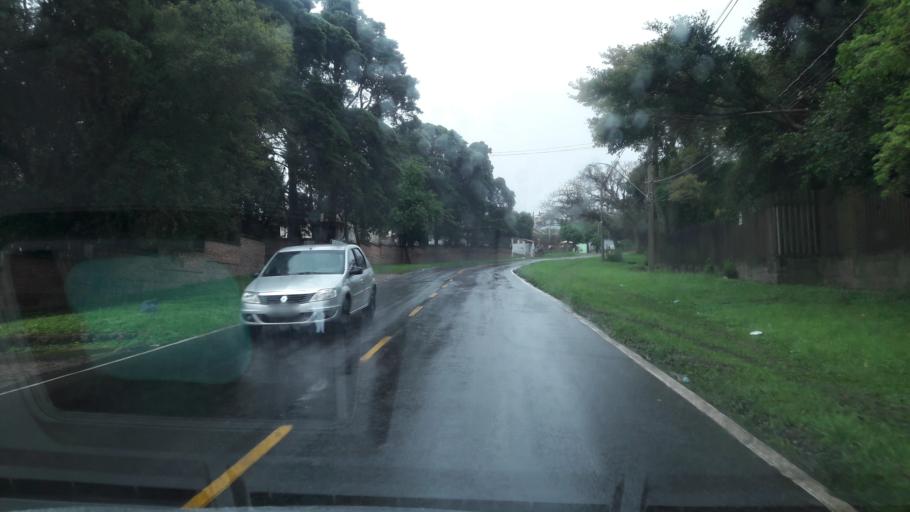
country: BR
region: Rio Grande do Sul
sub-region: Porto Alegre
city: Porto Alegre
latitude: -30.1298
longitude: -51.2234
